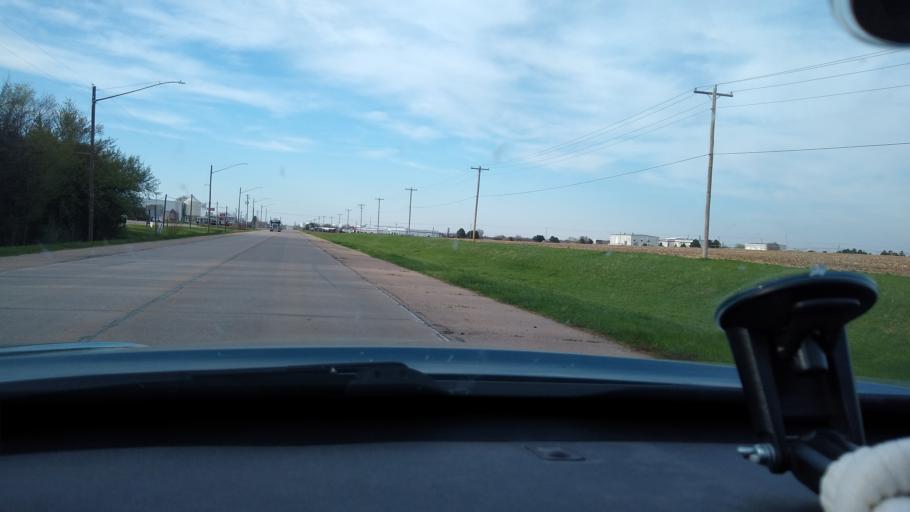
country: US
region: Nebraska
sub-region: Fillmore County
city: Geneva
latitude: 40.5346
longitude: -97.5958
